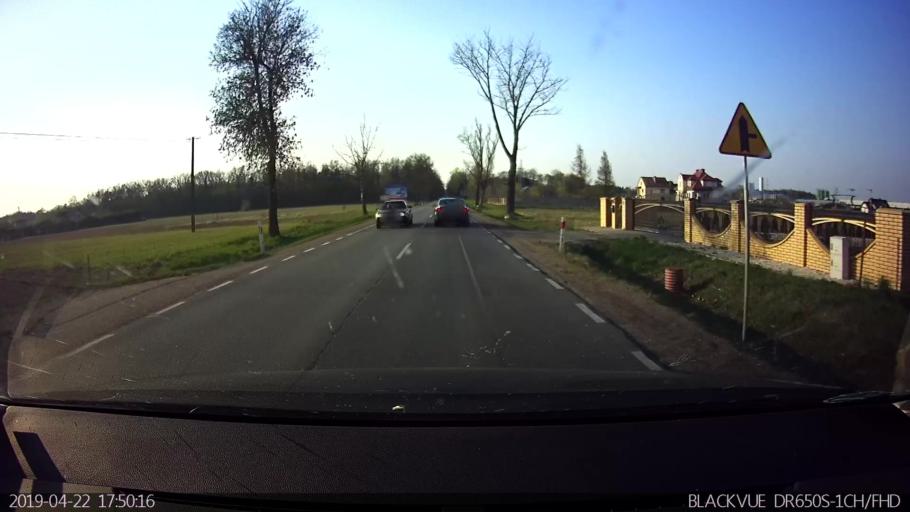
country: PL
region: Masovian Voivodeship
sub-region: Powiat wegrowski
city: Wegrow
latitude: 52.4226
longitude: 22.0031
